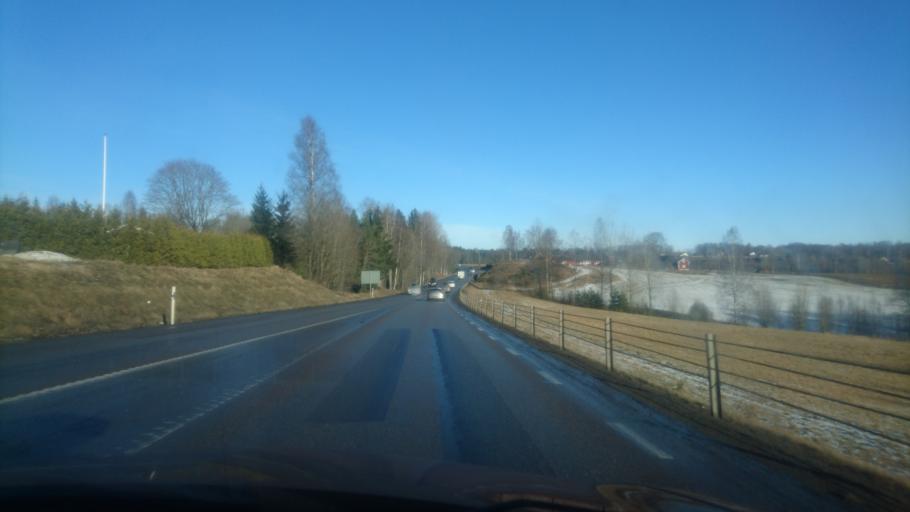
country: SE
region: Vaermland
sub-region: Sunne Kommun
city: Sunne
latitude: 59.7788
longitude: 13.0973
